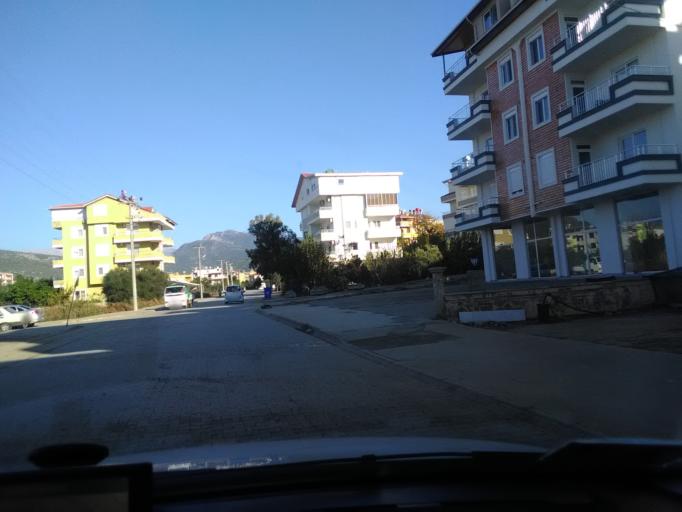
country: TR
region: Antalya
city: Gazipasa
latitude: 36.2659
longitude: 32.3204
